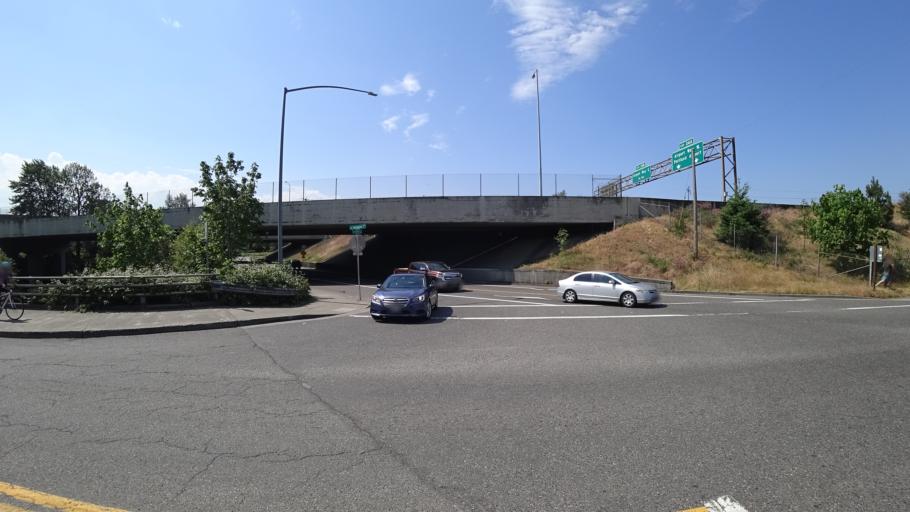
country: US
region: Oregon
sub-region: Multnomah County
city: Lents
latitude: 45.5668
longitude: -122.5541
